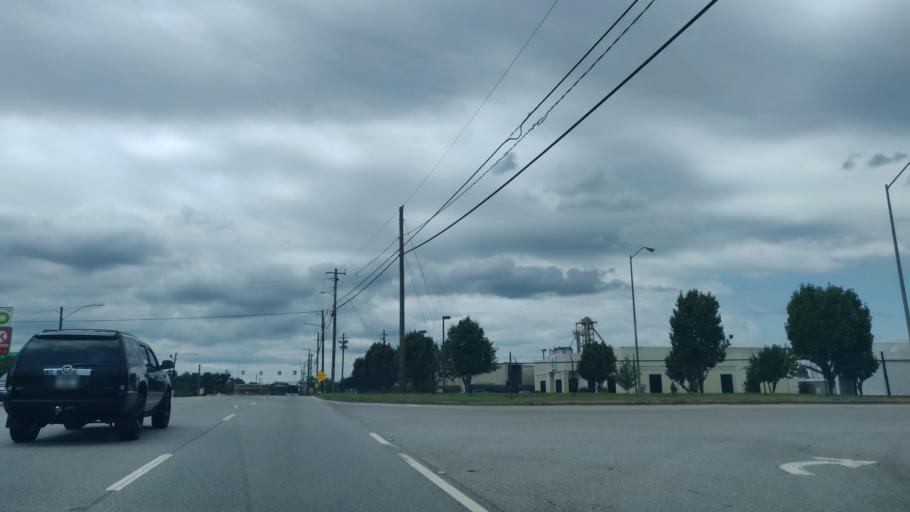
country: US
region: Georgia
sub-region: Terrell County
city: Dawson
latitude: 31.7835
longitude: -84.4465
